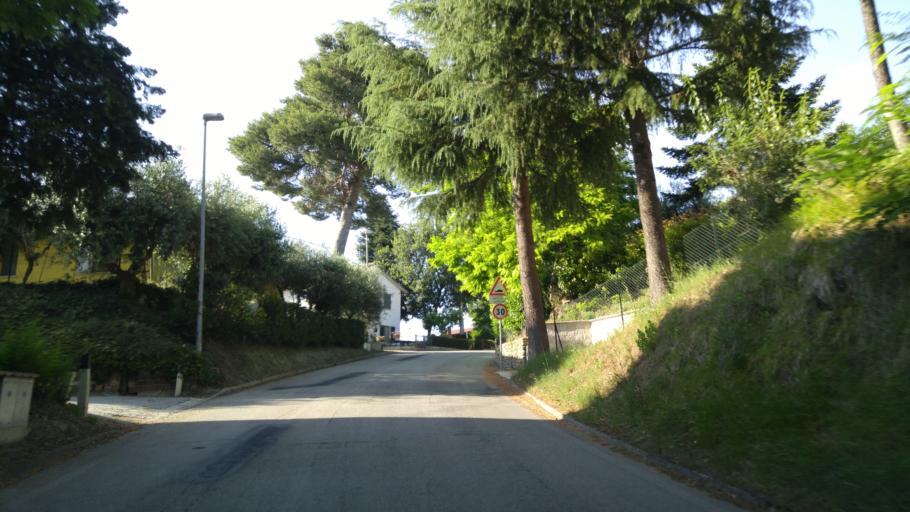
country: IT
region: The Marches
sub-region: Provincia di Pesaro e Urbino
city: Sant'Ippolito
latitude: 43.6883
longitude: 12.8719
